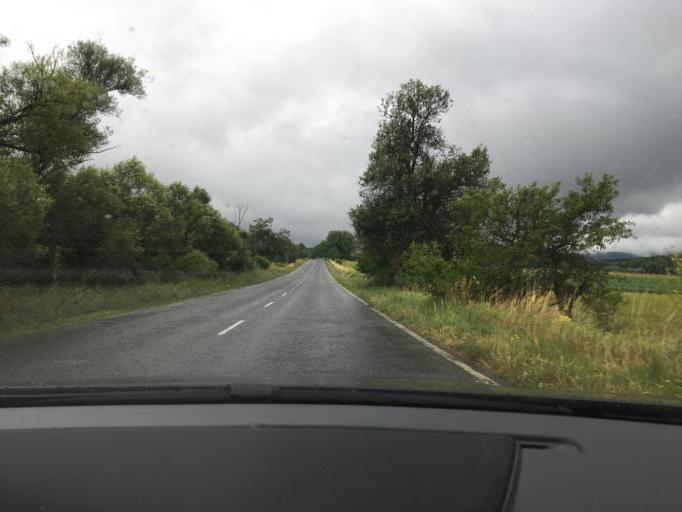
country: BG
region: Kyustendil
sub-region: Obshtina Kyustendil
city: Kyustendil
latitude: 42.2431
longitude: 22.5159
